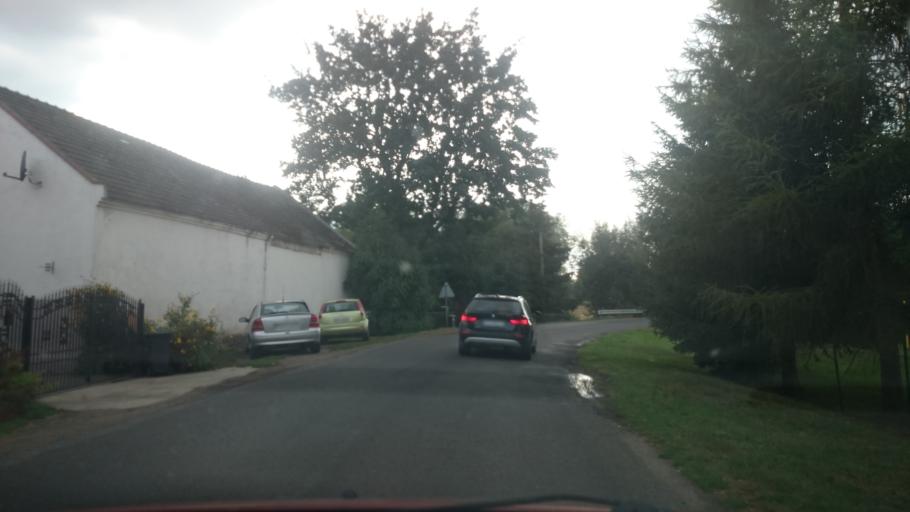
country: PL
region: Opole Voivodeship
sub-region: Powiat nyski
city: Otmuchow
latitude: 50.4996
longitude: 17.2169
